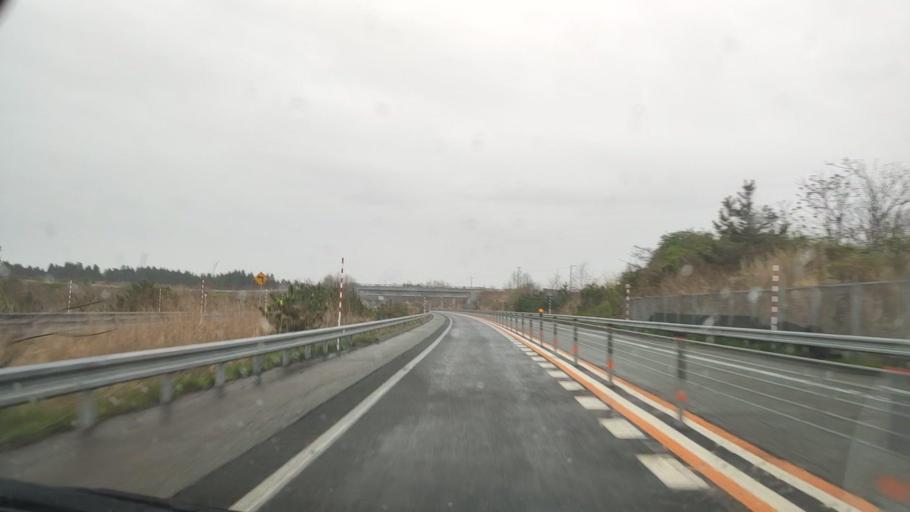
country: JP
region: Akita
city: Noshiromachi
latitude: 40.1542
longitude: 140.0230
